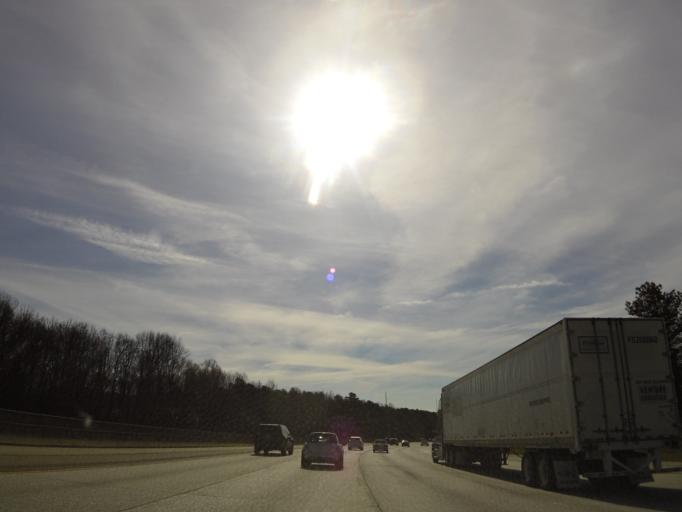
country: US
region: Georgia
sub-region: Fulton County
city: Union City
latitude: 33.6039
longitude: -84.4865
